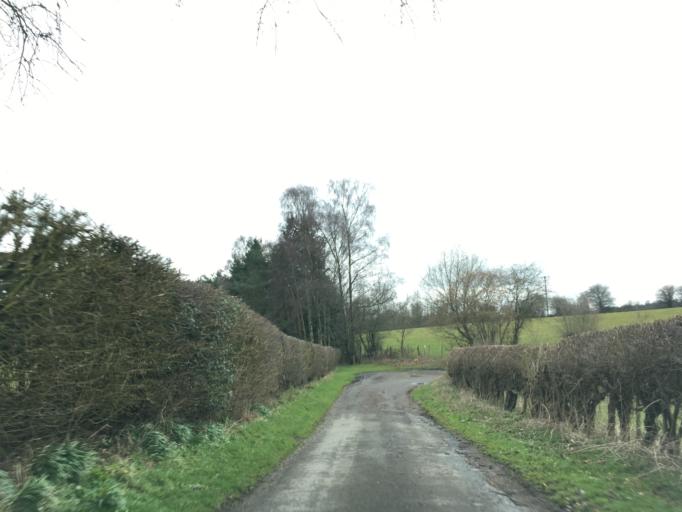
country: GB
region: England
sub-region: West Berkshire
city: Lambourn
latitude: 51.4755
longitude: -1.5364
